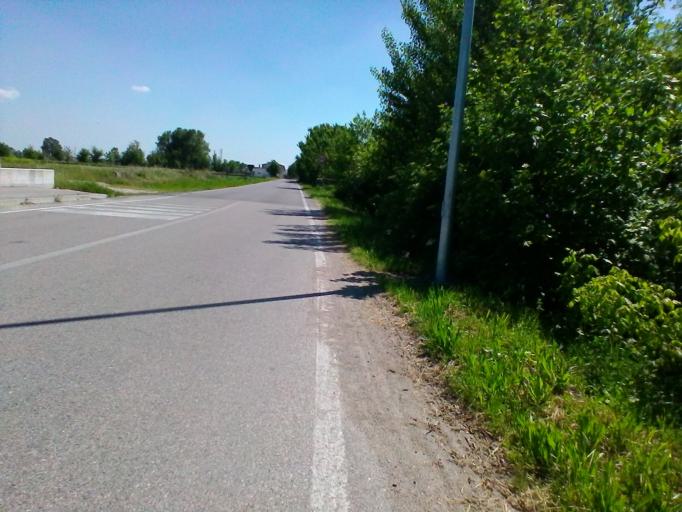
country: IT
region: Veneto
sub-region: Provincia di Verona
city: Povegliano Veronese
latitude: 45.3406
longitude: 10.8803
